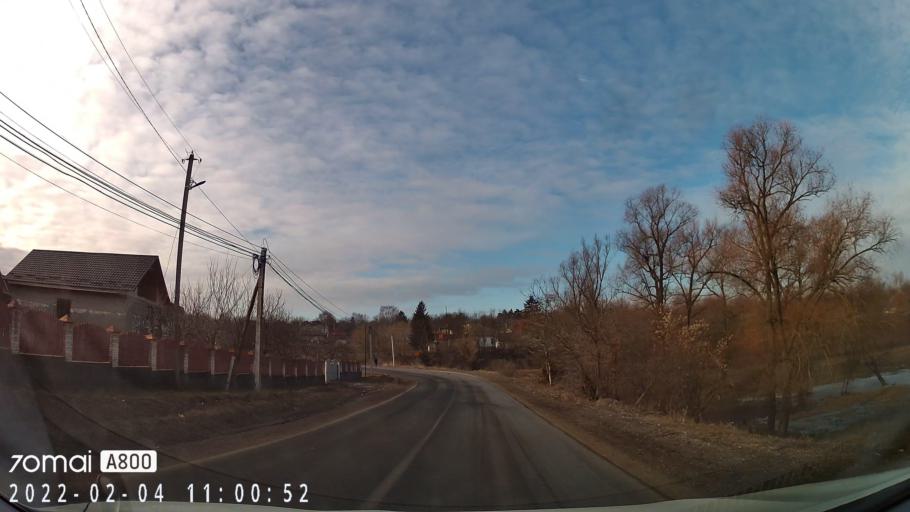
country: RO
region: Botosani
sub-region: Comuna Radauti-Prut
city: Miorcani
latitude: 48.2972
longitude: 26.9386
